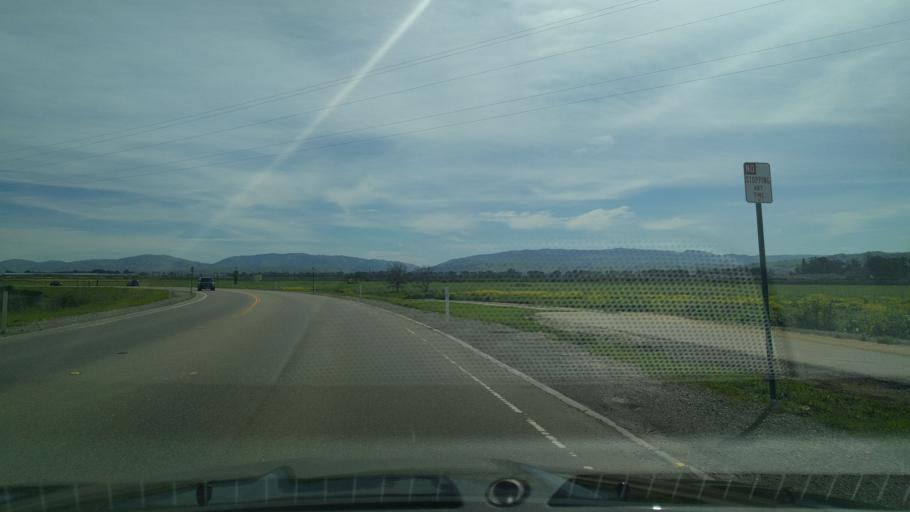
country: US
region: California
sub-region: Alameda County
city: Pleasanton
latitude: 37.6922
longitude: -121.8363
